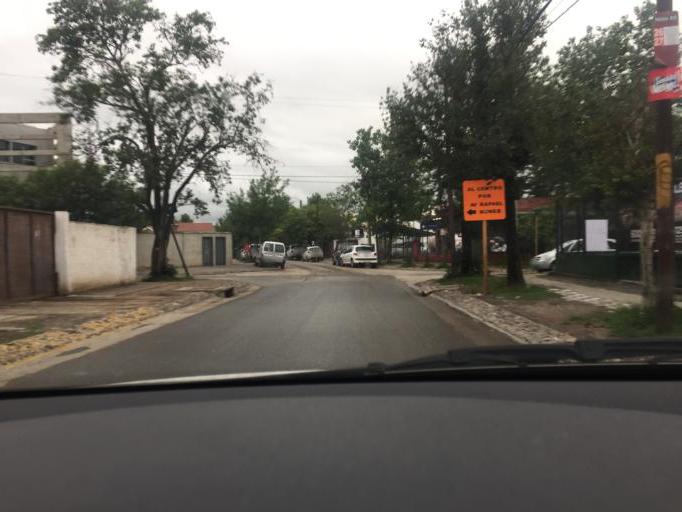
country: AR
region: Cordoba
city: Villa Allende
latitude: -31.3573
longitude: -64.2431
